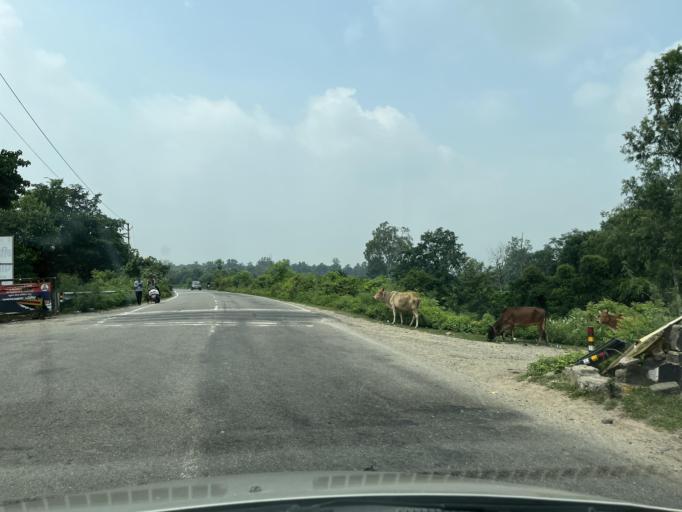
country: IN
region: Uttarakhand
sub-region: Haridwar
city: Sultanpur
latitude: 29.7616
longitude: 78.2721
